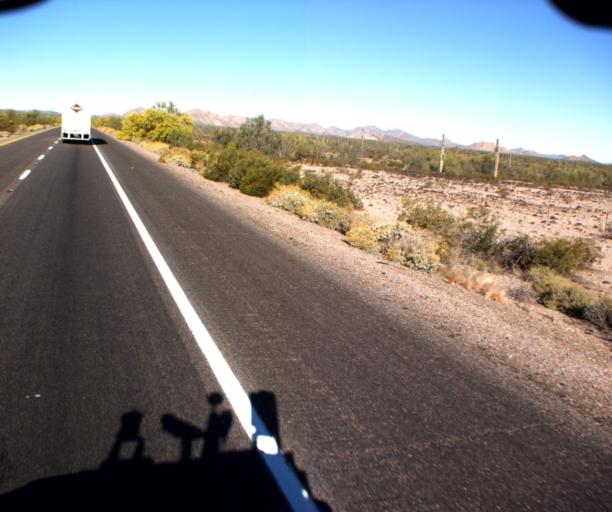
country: US
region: Arizona
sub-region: Pinal County
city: Maricopa
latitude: 32.8322
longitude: -112.0657
